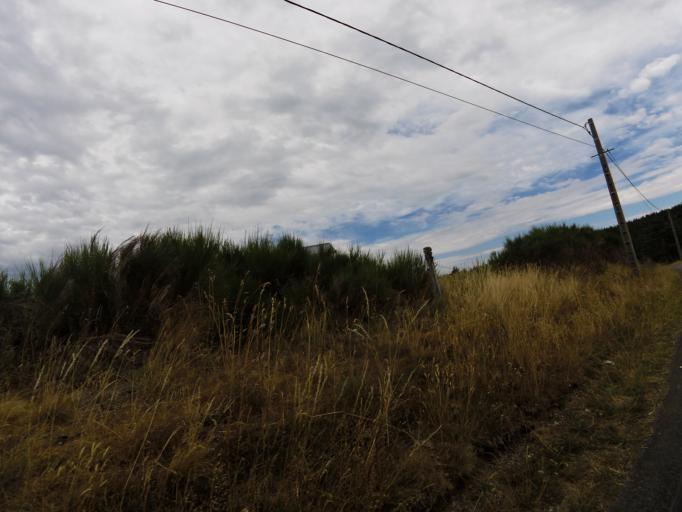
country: FR
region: Languedoc-Roussillon
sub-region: Departement du Gard
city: Valleraugue
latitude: 44.0908
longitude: 3.5514
